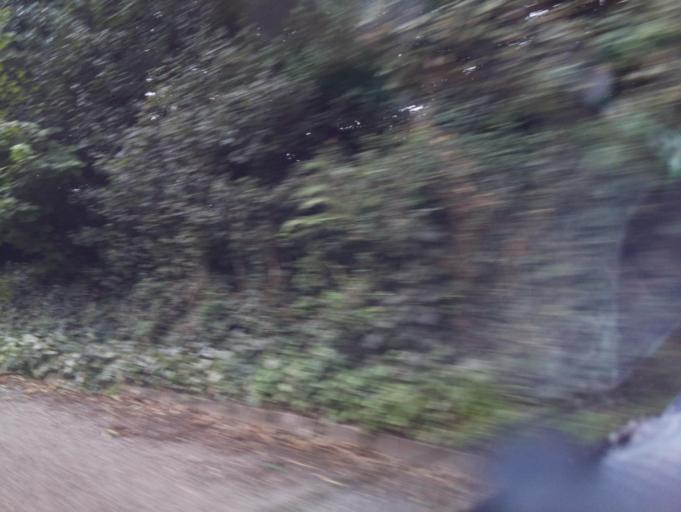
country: GB
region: England
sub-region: Staffordshire
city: Cheadle
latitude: 53.0245
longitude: -1.9571
